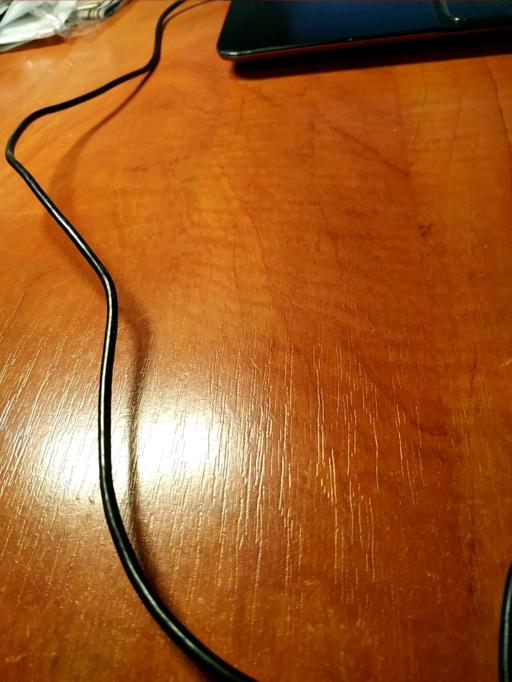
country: BY
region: Mogilev
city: Khotsimsk
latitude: 53.5389
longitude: 32.4992
